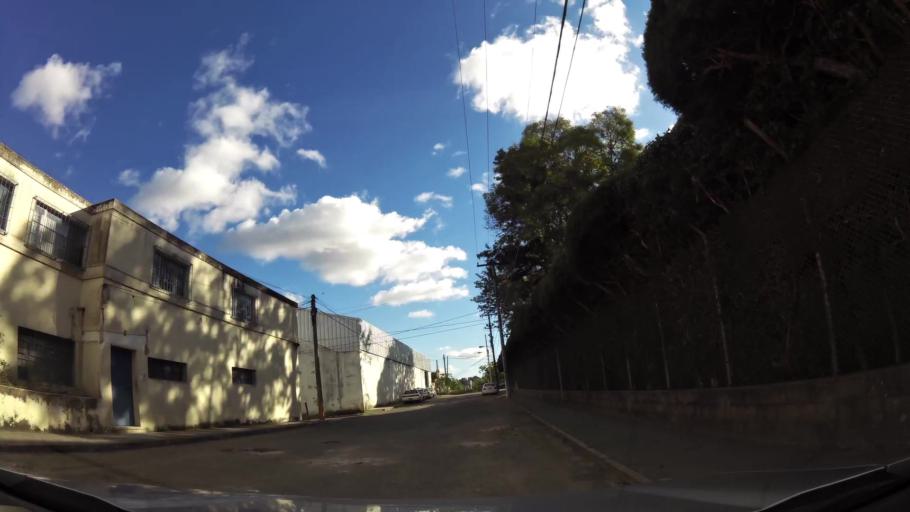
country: GT
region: Guatemala
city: Guatemala City
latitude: 14.6329
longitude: -90.5011
